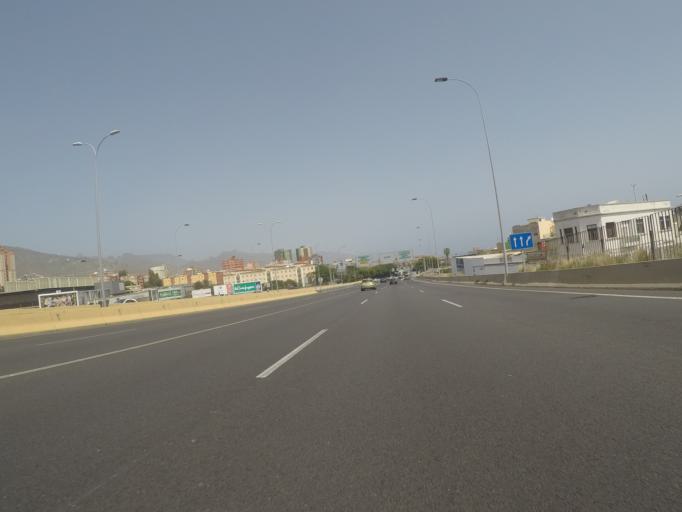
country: ES
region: Canary Islands
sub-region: Provincia de Santa Cruz de Tenerife
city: Santa Cruz de Tenerife
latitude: 28.4554
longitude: -16.2688
